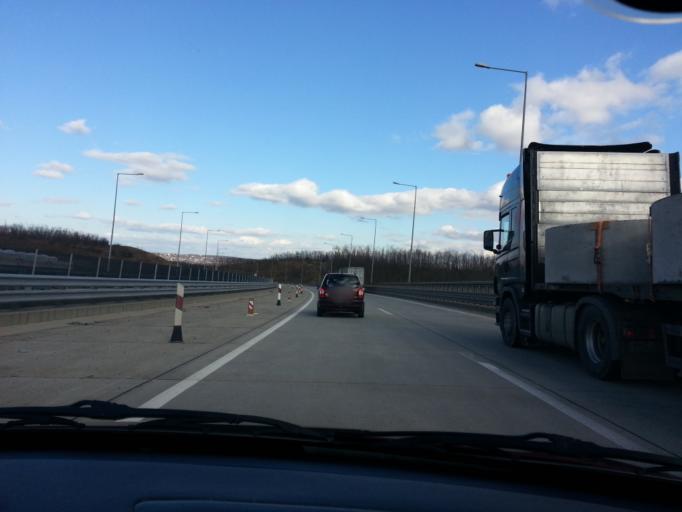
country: HU
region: Pest
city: Godollo
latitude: 47.5670
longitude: 19.3248
